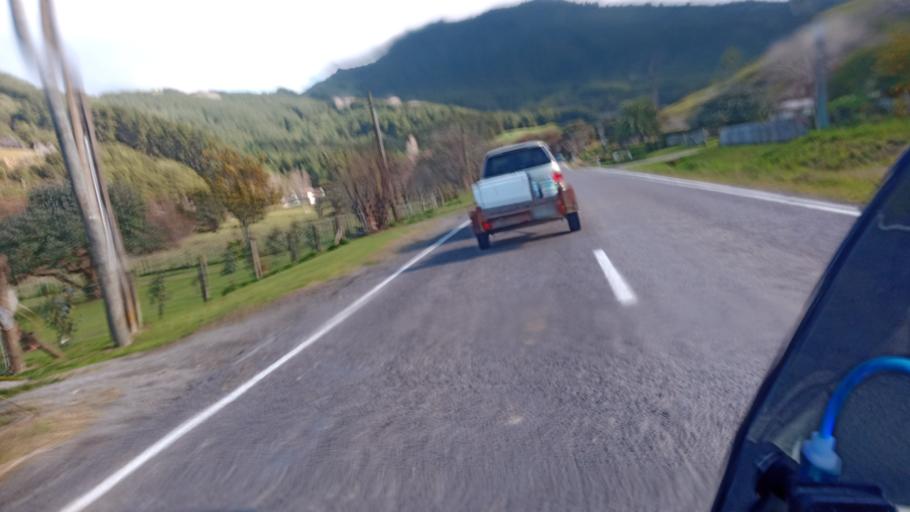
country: NZ
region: Gisborne
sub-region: Gisborne District
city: Gisborne
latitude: -38.1169
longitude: 178.3016
